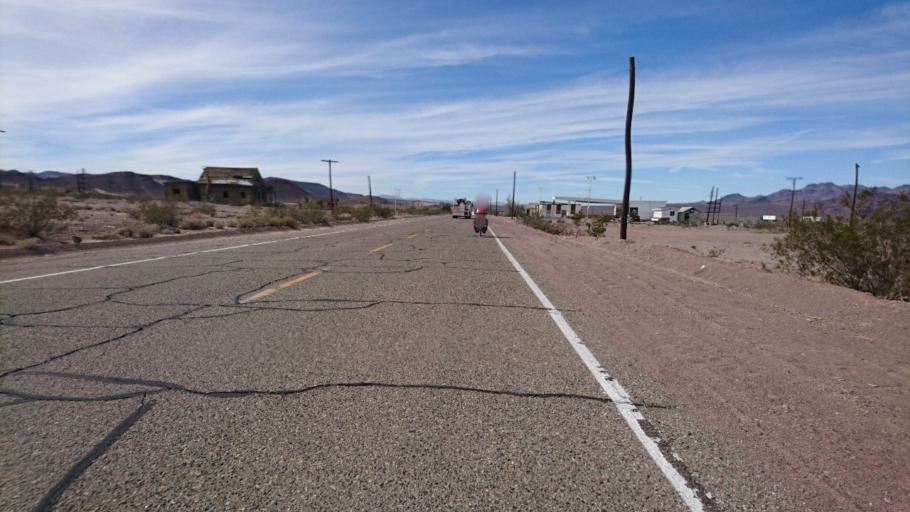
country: US
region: California
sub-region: San Bernardino County
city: Twentynine Palms
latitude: 34.7239
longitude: -116.1571
